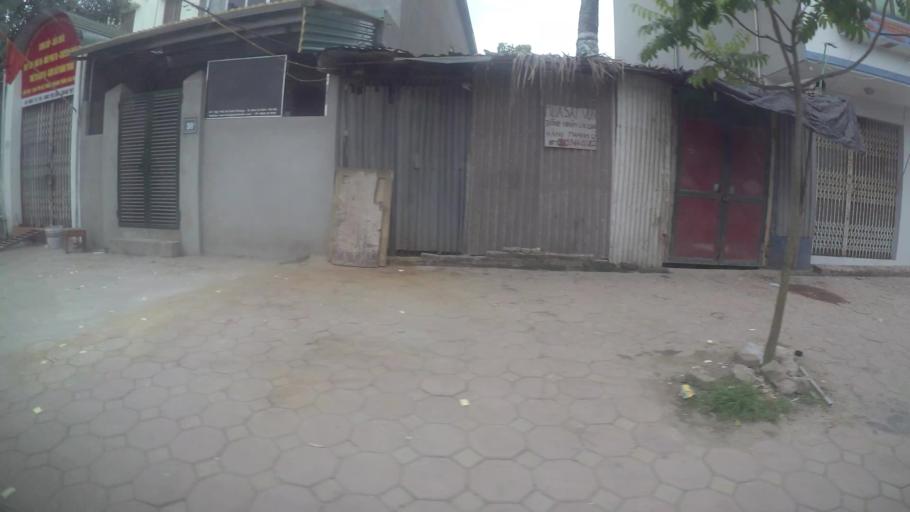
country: VN
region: Ha Noi
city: Cau Dien
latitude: 21.0364
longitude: 105.7411
